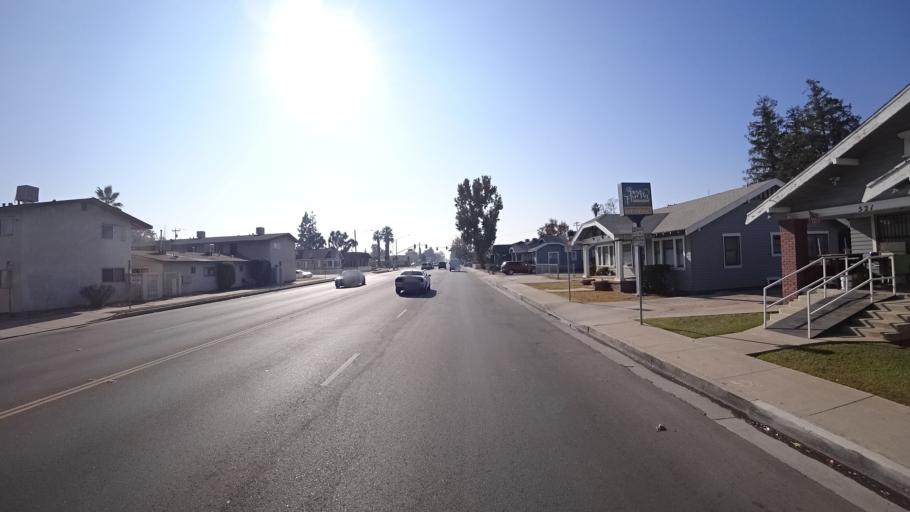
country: US
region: California
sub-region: Kern County
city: Bakersfield
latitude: 35.3623
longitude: -119.0213
